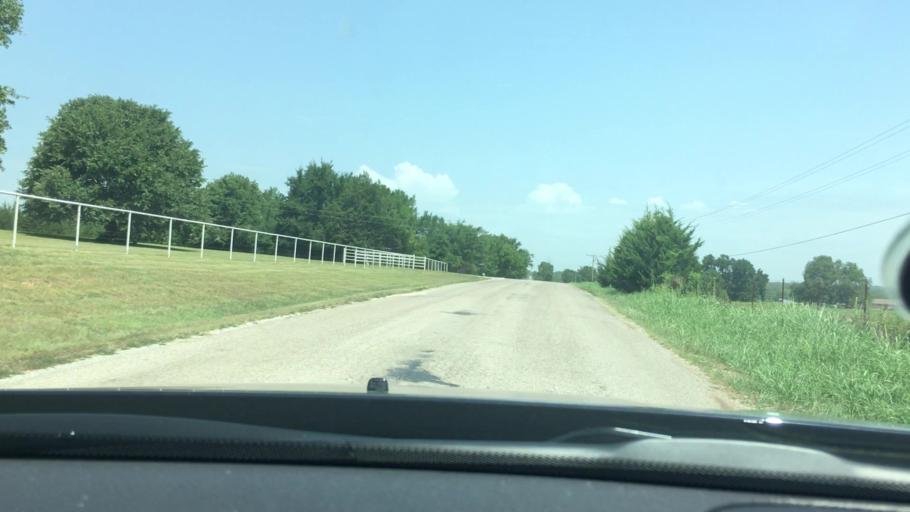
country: US
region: Oklahoma
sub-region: Pontotoc County
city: Byng
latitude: 34.8296
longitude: -96.6698
